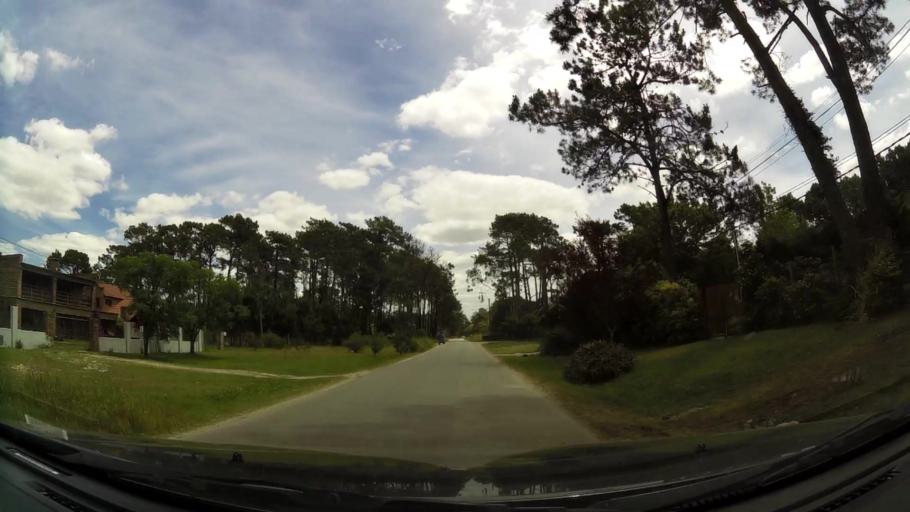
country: UY
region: Canelones
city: Pando
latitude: -34.7967
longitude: -55.8959
